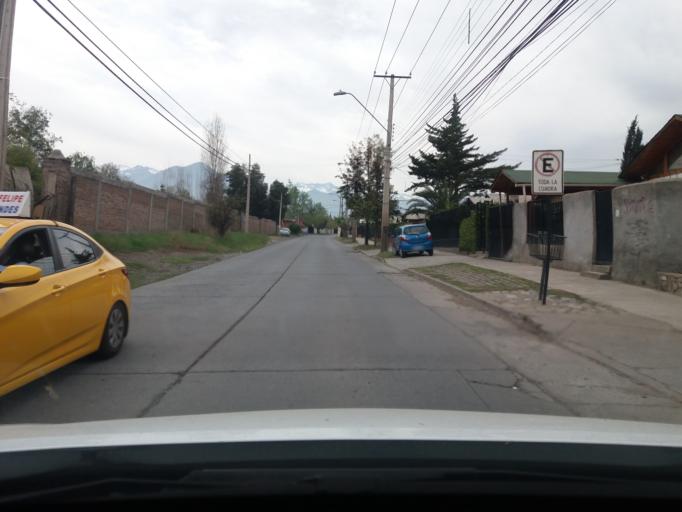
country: CL
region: Valparaiso
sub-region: Provincia de Los Andes
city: Los Andes
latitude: -32.8314
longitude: -70.6142
